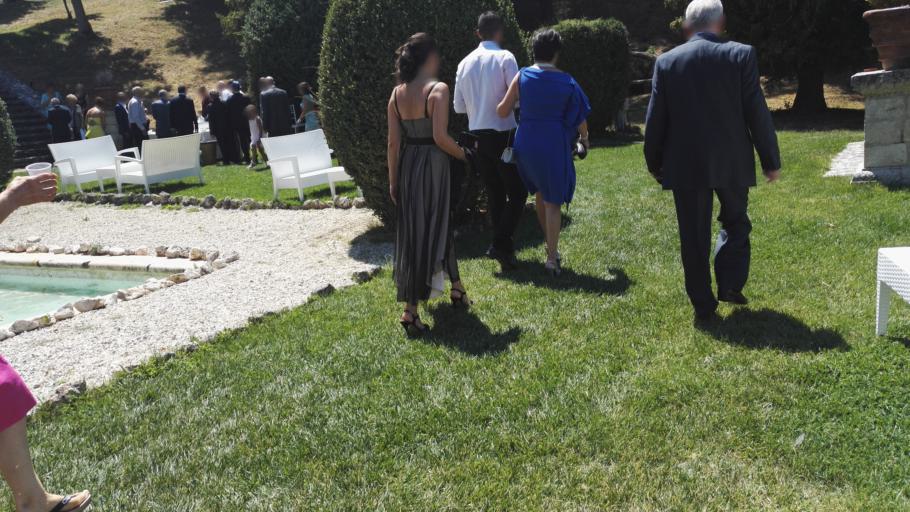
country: IT
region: Calabria
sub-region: Provincia di Cosenza
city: Carolei
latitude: 39.2493
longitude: 16.2190
